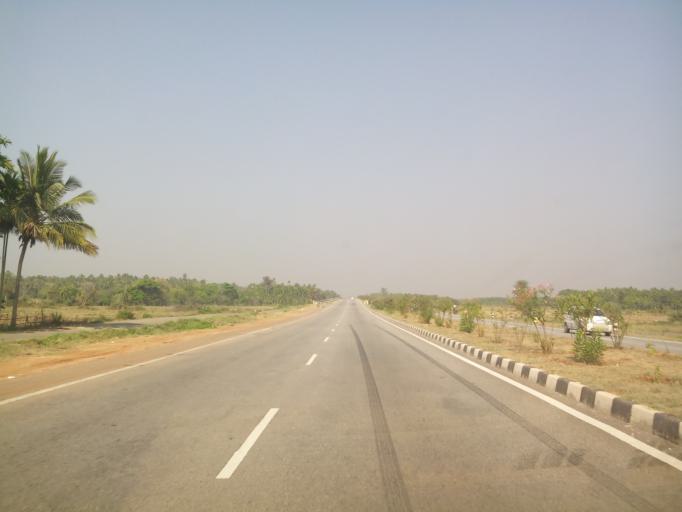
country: IN
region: Karnataka
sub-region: Tumkur
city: Kunigal
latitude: 13.0051
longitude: 76.9972
